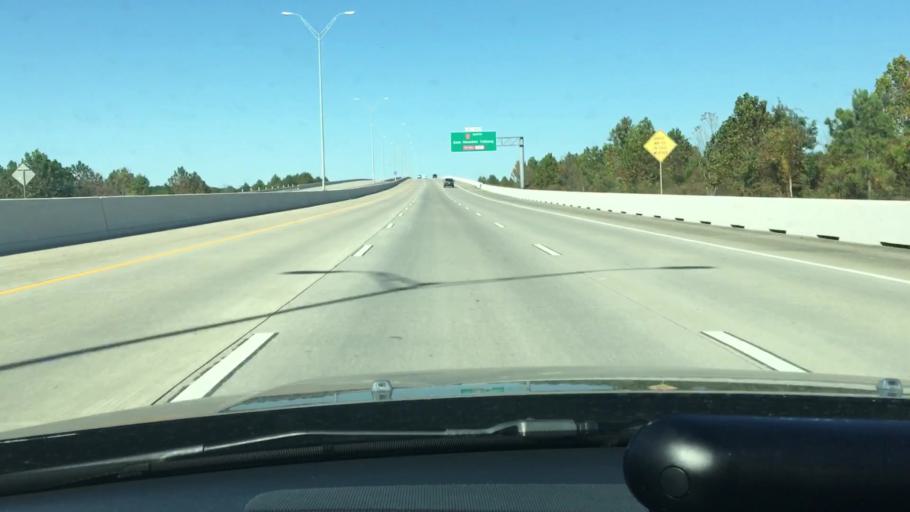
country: US
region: Texas
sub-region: Harris County
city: Cloverleaf
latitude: 29.8281
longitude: -95.1713
